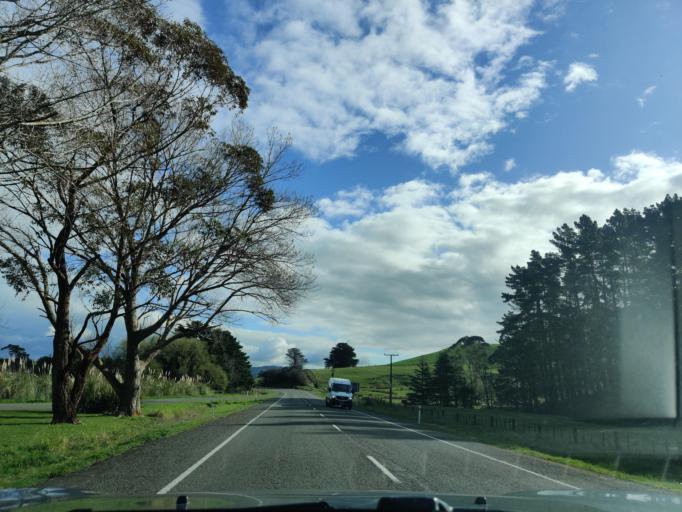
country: NZ
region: Manawatu-Wanganui
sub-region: Palmerston North City
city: Palmerston North
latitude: -40.3385
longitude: 175.8918
